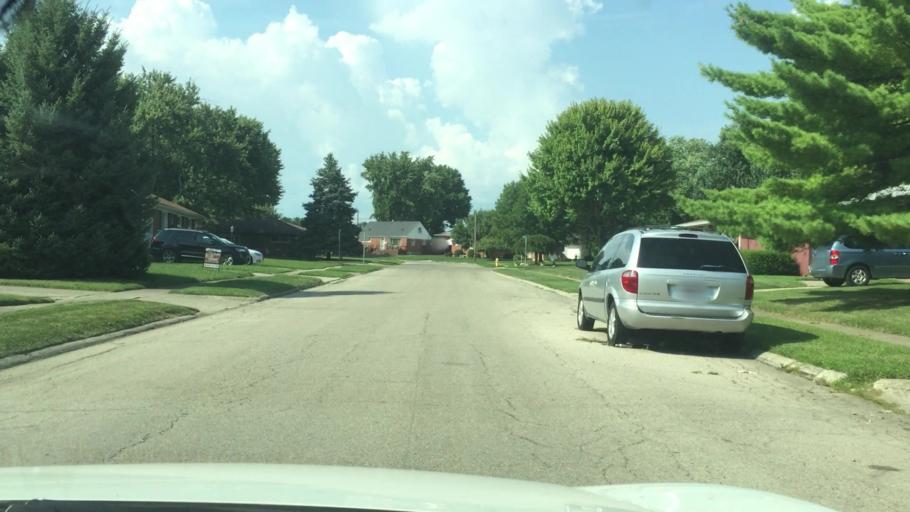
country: US
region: Ohio
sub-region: Clark County
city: Northridge
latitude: 39.9936
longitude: -83.7780
